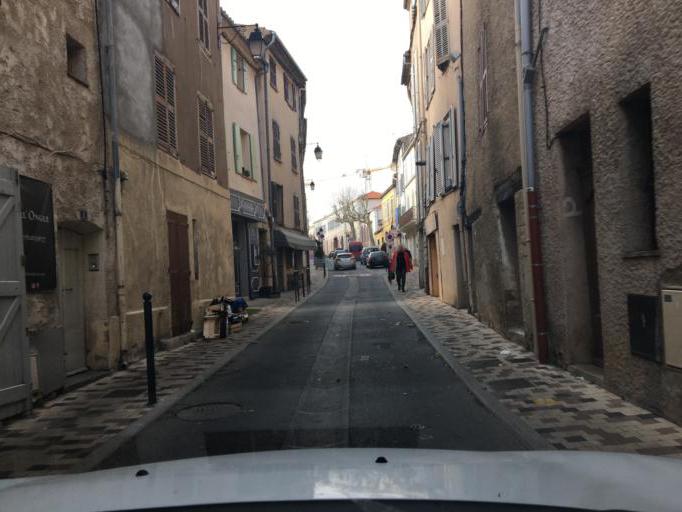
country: FR
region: Provence-Alpes-Cote d'Azur
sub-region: Departement du Var
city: Flayosc
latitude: 43.5340
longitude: 6.3963
